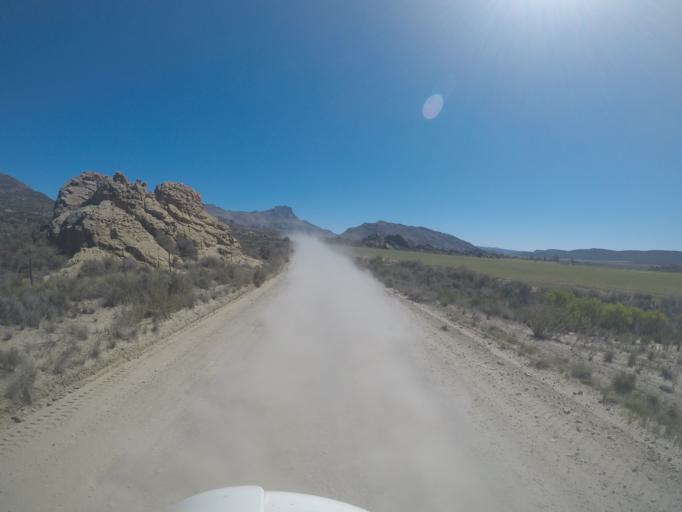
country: ZA
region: Western Cape
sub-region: Cape Winelands District Municipality
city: Ceres
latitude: -32.8797
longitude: 19.4492
